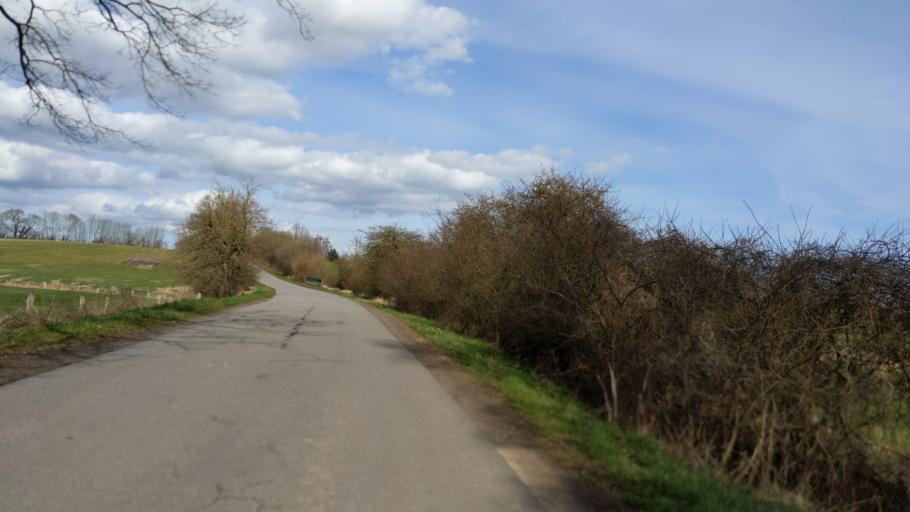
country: DE
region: Schleswig-Holstein
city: Susel
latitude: 54.0674
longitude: 10.6594
